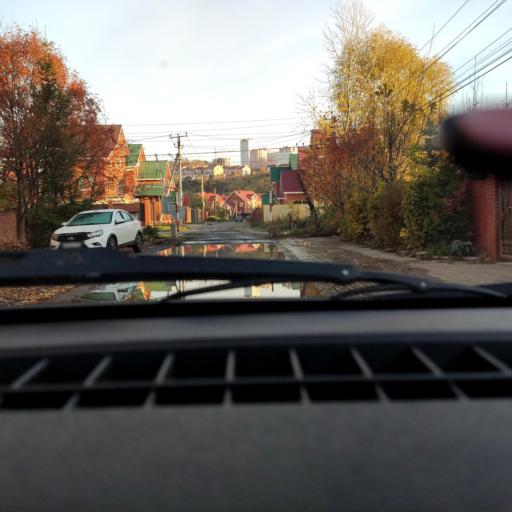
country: RU
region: Bashkortostan
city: Ufa
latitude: 54.6907
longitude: 55.9776
